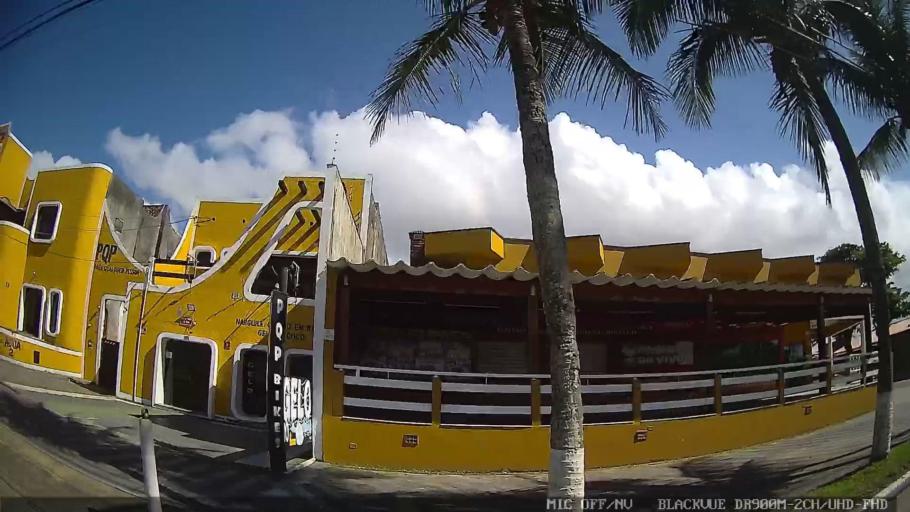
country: BR
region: Sao Paulo
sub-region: Peruibe
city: Peruibe
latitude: -24.3216
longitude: -46.9925
